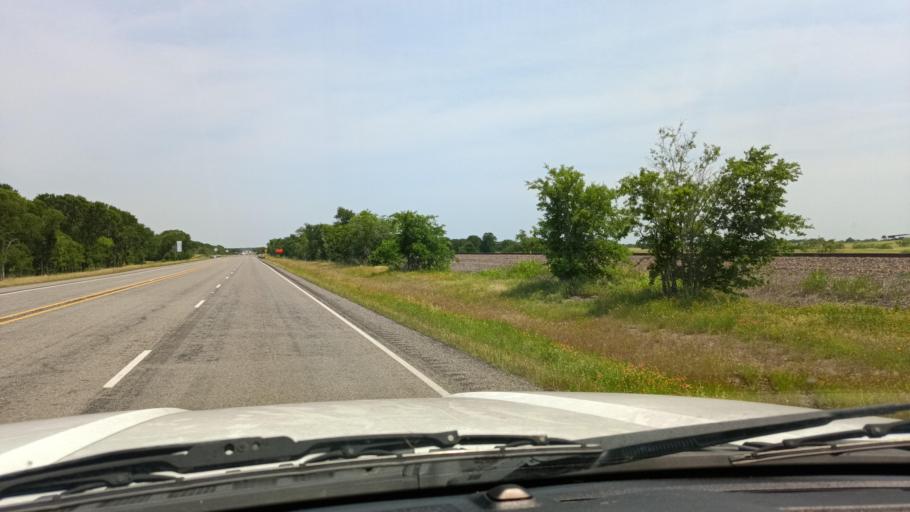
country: US
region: Texas
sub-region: Bell County
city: Rogers
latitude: 30.9013
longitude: -97.1735
